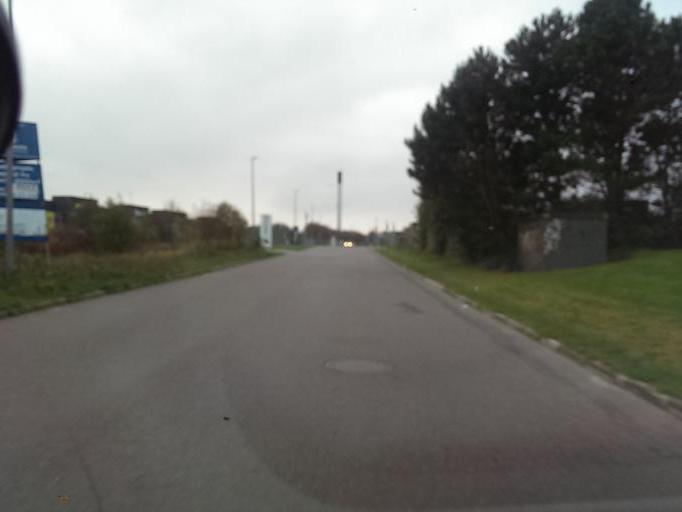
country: DK
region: South Denmark
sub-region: Esbjerg Kommune
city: Esbjerg
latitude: 55.5056
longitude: 8.4560
